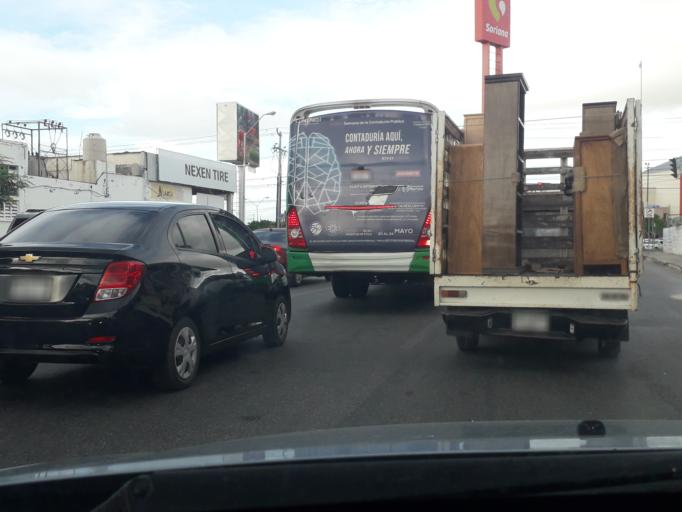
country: MX
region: Yucatan
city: Caucel
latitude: 20.9889
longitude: -89.6639
